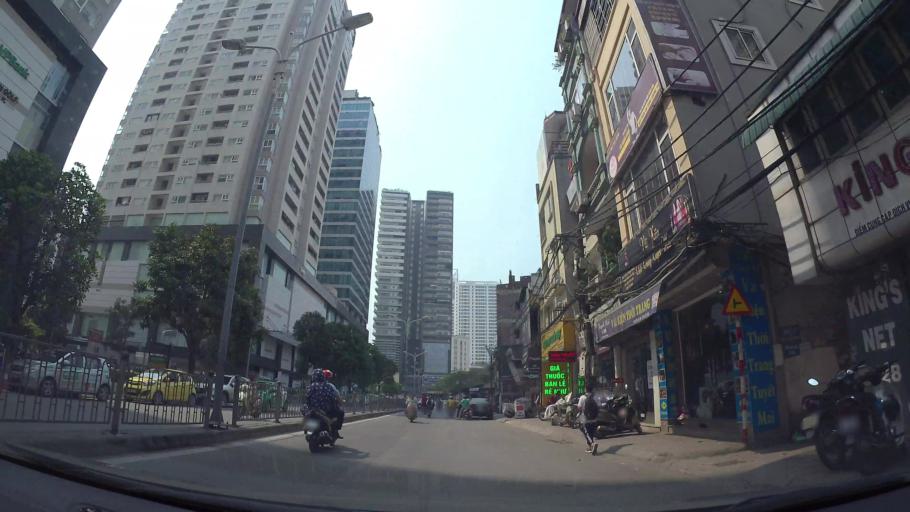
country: VN
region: Ha Noi
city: Thanh Xuan
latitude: 21.0014
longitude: 105.8067
